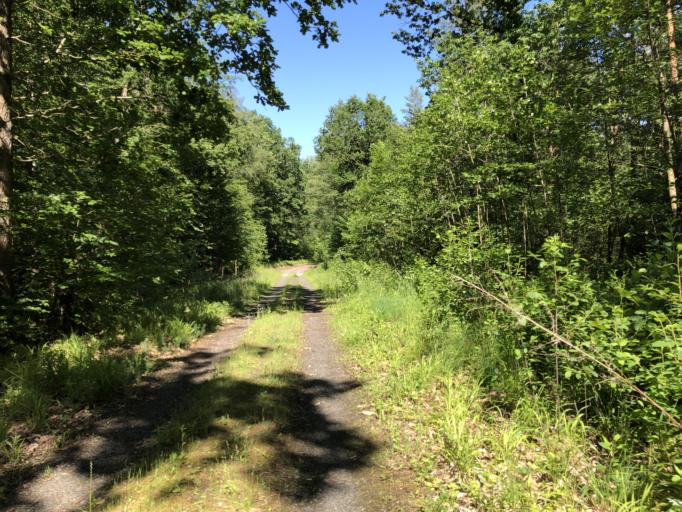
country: DE
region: Bavaria
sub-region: Upper Franconia
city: Memmelsdorf
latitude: 49.9188
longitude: 10.9597
